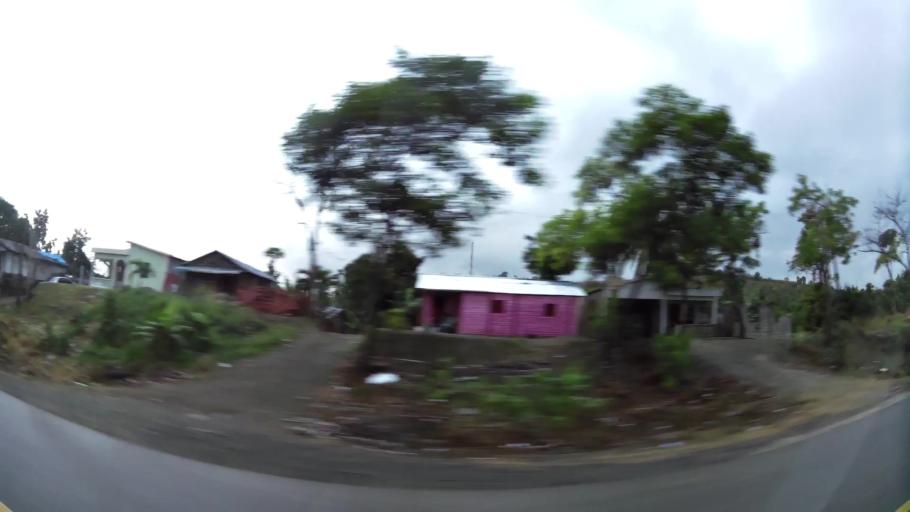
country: DO
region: San Cristobal
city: Villa Altagracia
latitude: 18.6018
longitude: -70.1354
